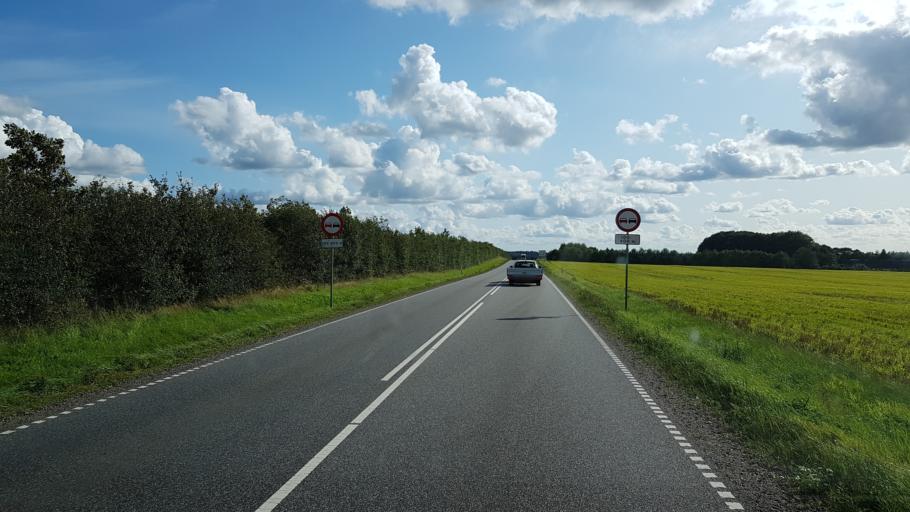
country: DK
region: South Denmark
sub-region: Billund Kommune
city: Grindsted
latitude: 55.7052
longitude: 8.9781
